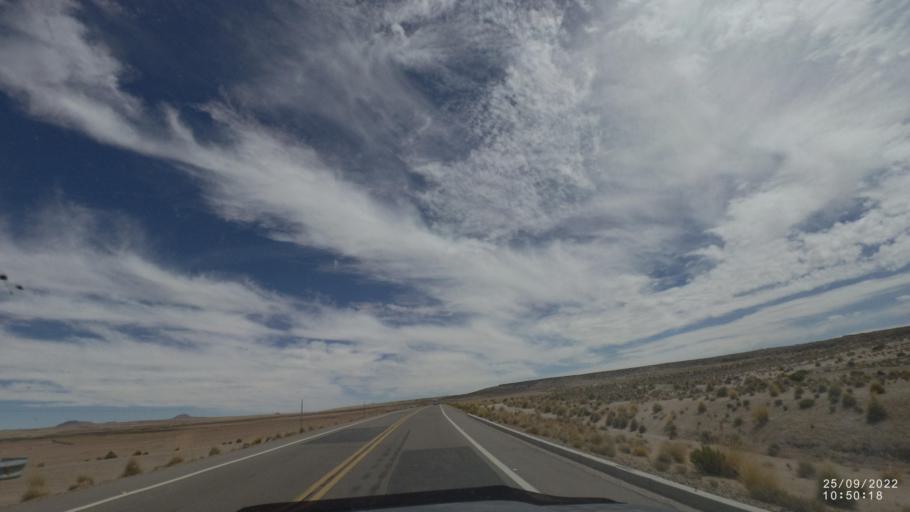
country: BO
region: Oruro
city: Challapata
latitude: -19.5776
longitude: -66.8366
